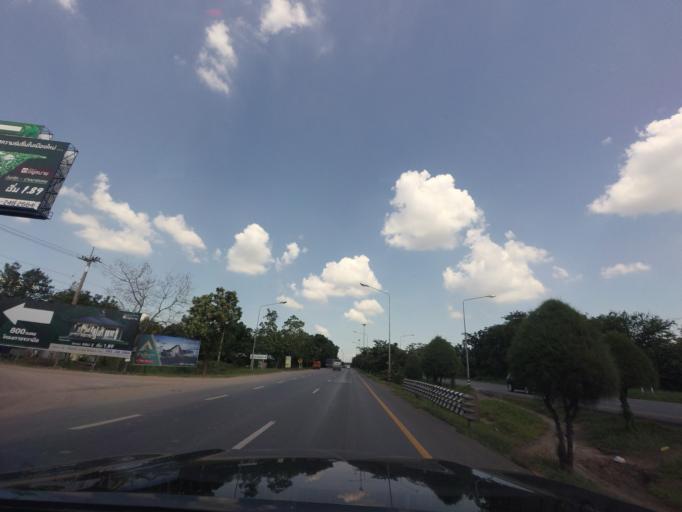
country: TH
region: Nakhon Ratchasima
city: Nakhon Ratchasima
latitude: 15.0559
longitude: 102.1541
